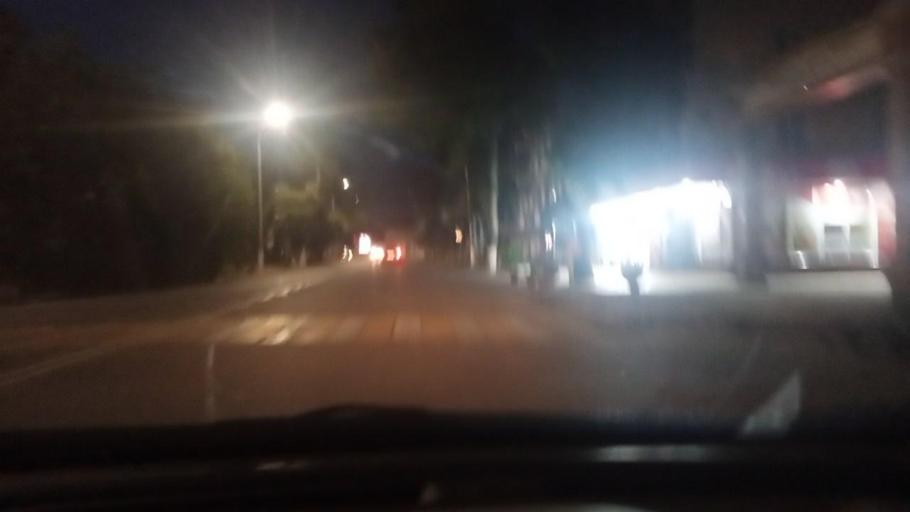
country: UZ
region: Toshkent Shahri
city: Tashkent
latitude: 41.2731
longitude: 69.2782
